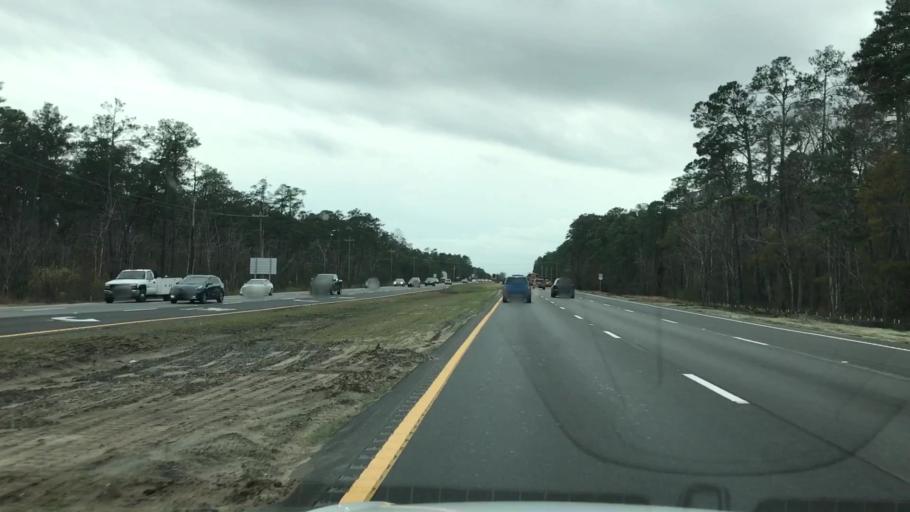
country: US
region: South Carolina
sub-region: Horry County
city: Garden City
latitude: 33.6148
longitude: -79.0089
